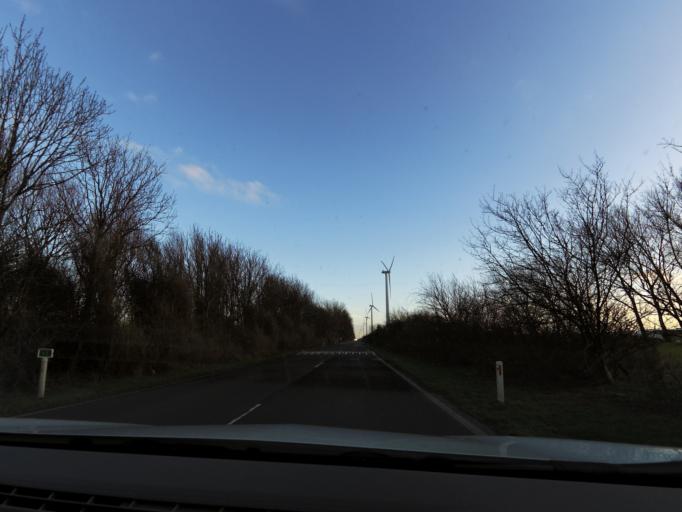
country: NL
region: South Holland
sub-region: Gemeente Rotterdam
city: Hoek van Holland
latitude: 51.9632
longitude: 4.1385
